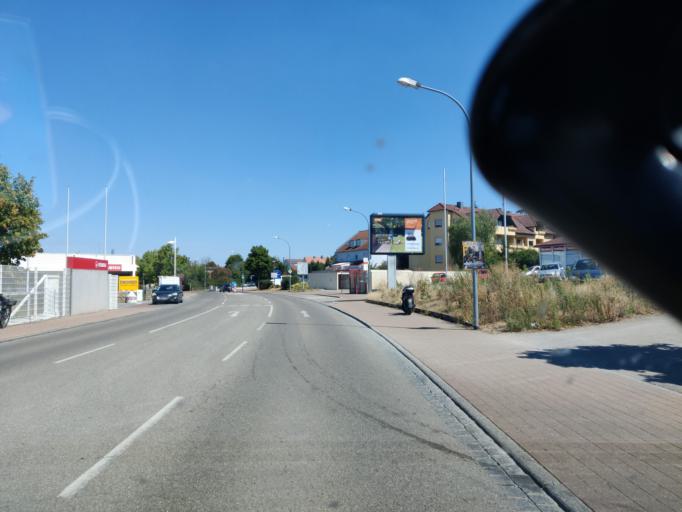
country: DE
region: Bavaria
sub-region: Regierungsbezirk Mittelfranken
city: Weissenburg in Bayern
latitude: 49.0215
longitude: 10.9658
